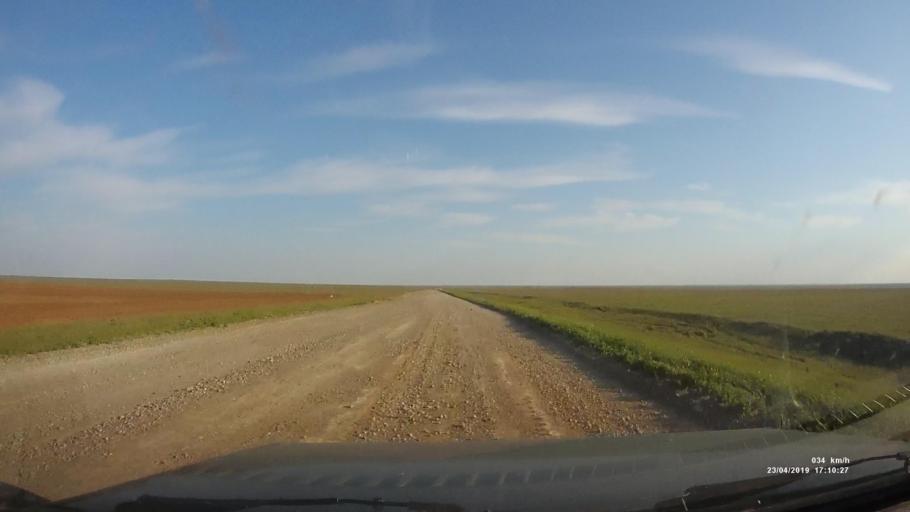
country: RU
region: Kalmykiya
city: Priyutnoye
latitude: 46.2467
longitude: 43.4841
